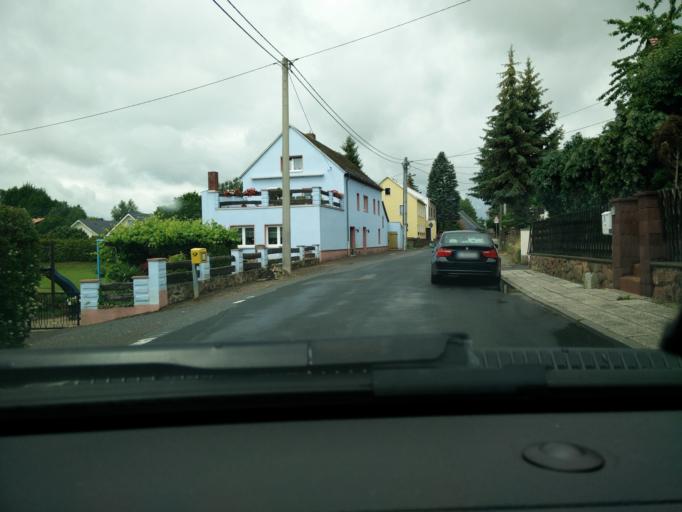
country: DE
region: Saxony
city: Geithain
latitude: 51.0875
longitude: 12.6887
